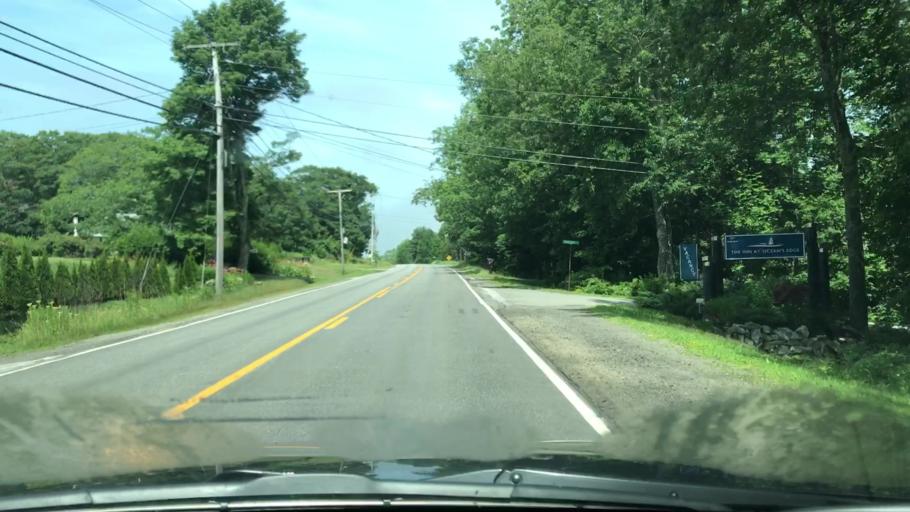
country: US
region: Maine
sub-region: Waldo County
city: Lincolnville
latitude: 44.2667
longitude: -69.0178
